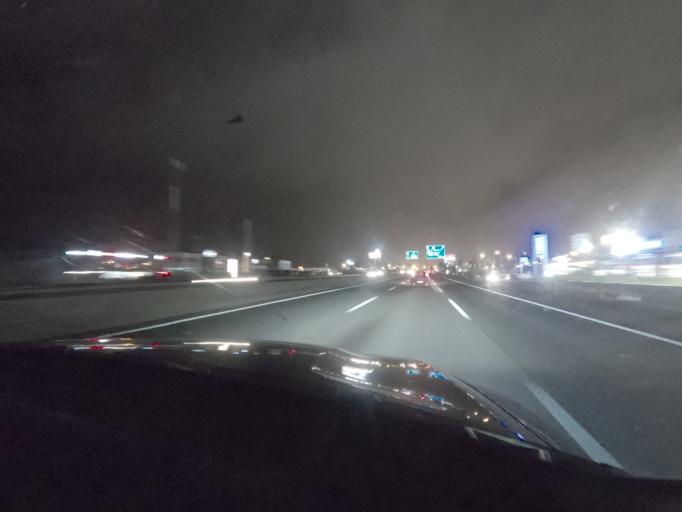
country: PT
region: Lisbon
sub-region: Vila Franca de Xira
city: Castanheira do Ribatejo
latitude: 38.9791
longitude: -8.9754
